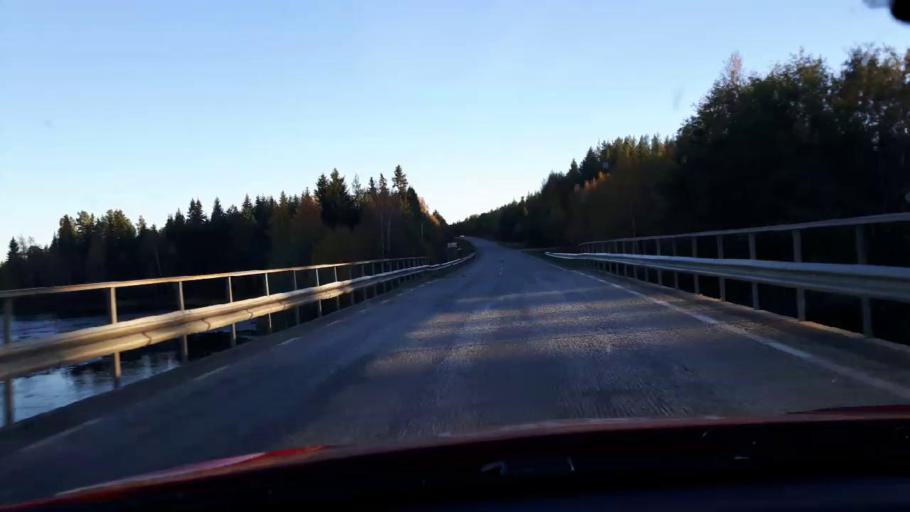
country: SE
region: Jaemtland
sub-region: Krokoms Kommun
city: Krokom
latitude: 63.4542
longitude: 14.4901
